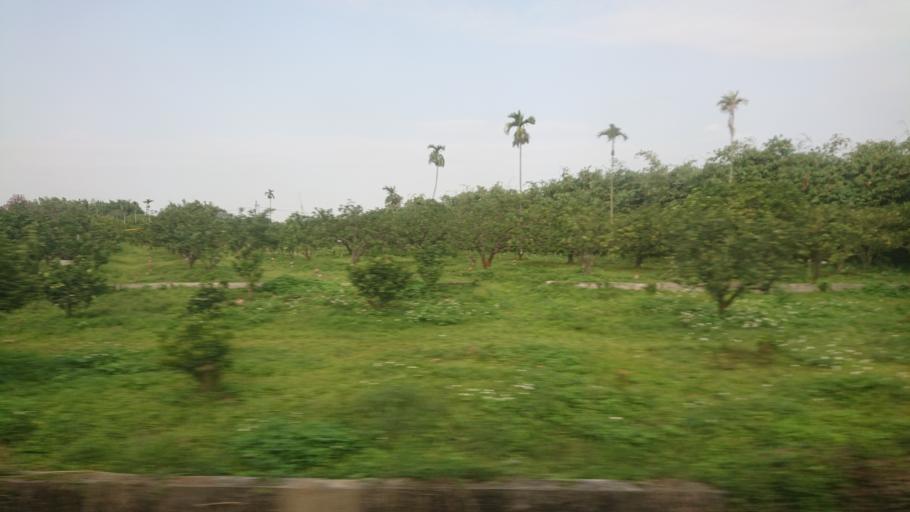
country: TW
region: Taiwan
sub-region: Yunlin
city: Douliu
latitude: 23.7207
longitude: 120.5685
